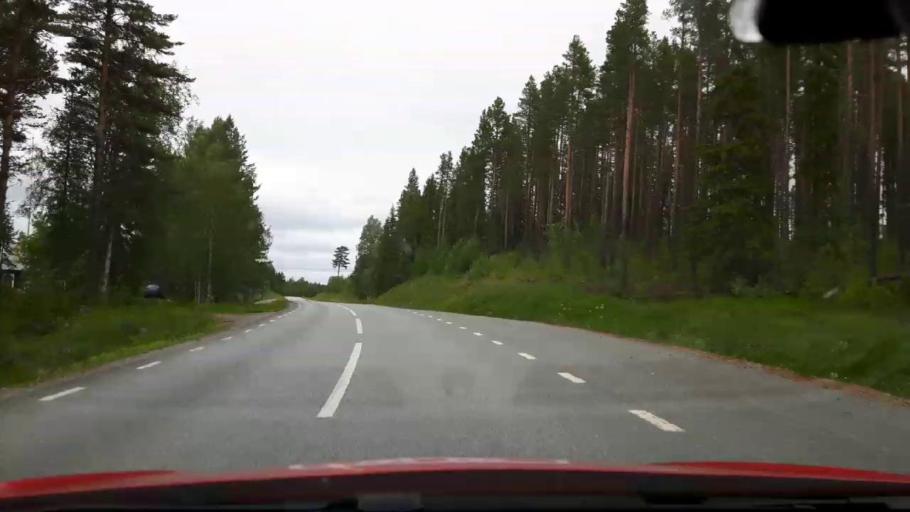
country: SE
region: Jaemtland
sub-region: OEstersunds Kommun
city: Lit
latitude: 63.7210
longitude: 14.7163
